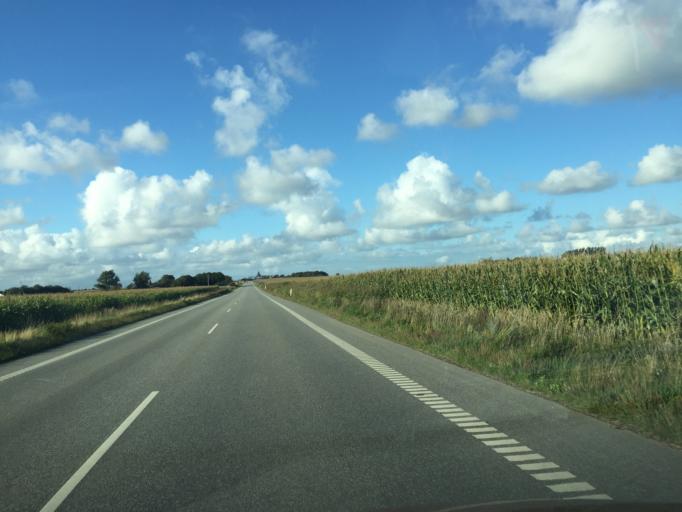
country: DE
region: Schleswig-Holstein
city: Rodenas
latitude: 54.9764
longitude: 8.6985
